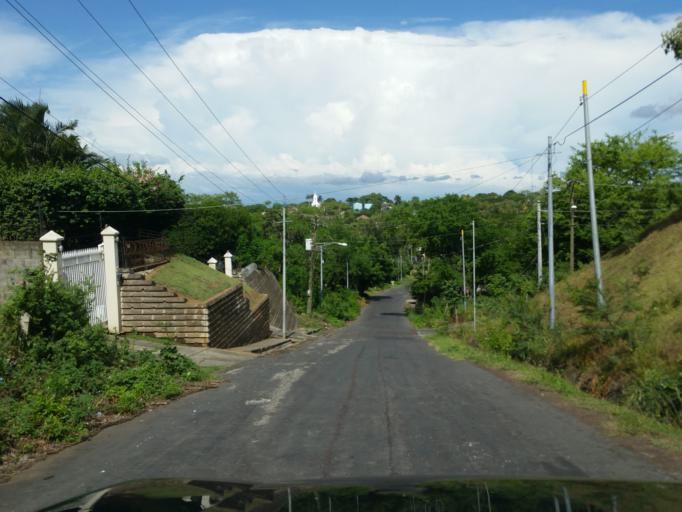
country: NI
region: Managua
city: Managua
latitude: 12.0853
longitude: -86.2478
